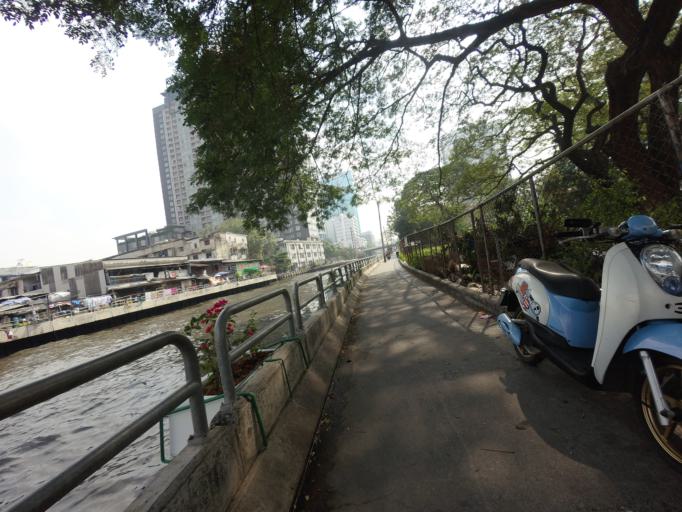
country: TH
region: Bangkok
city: Watthana
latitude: 13.7430
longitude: 100.5838
